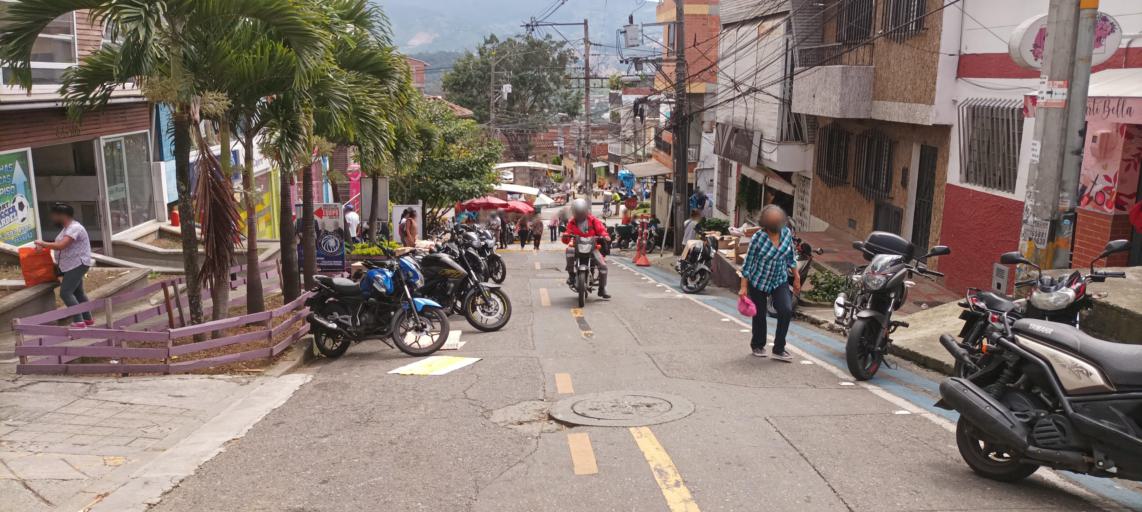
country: CO
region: Antioquia
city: Medellin
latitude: 6.2674
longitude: -75.5545
